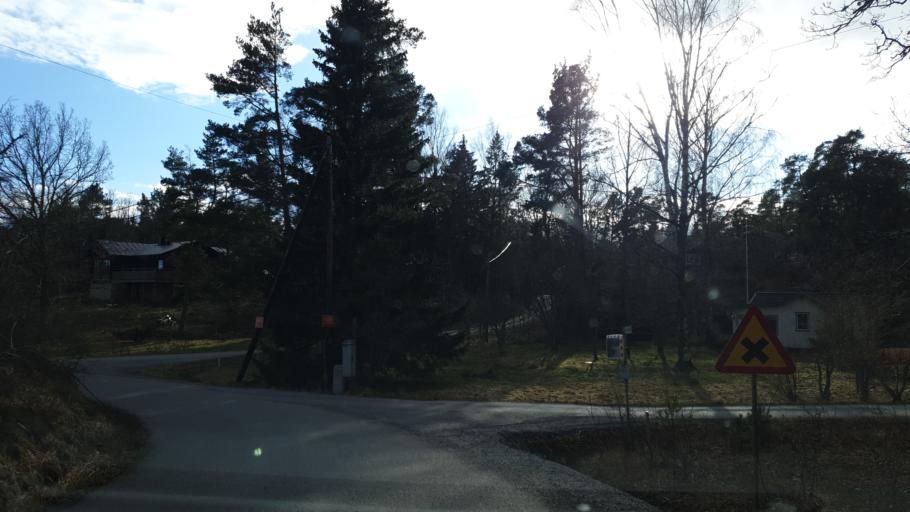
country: SE
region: Stockholm
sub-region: Varmdo Kommun
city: Holo
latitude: 59.3703
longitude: 18.6705
